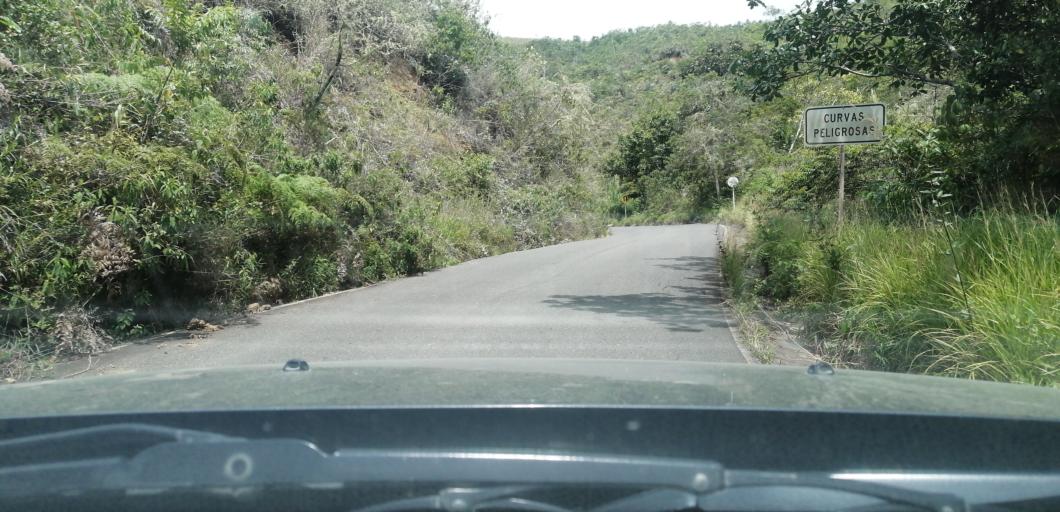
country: CO
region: Valle del Cauca
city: Dagua
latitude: 3.7131
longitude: -76.5840
